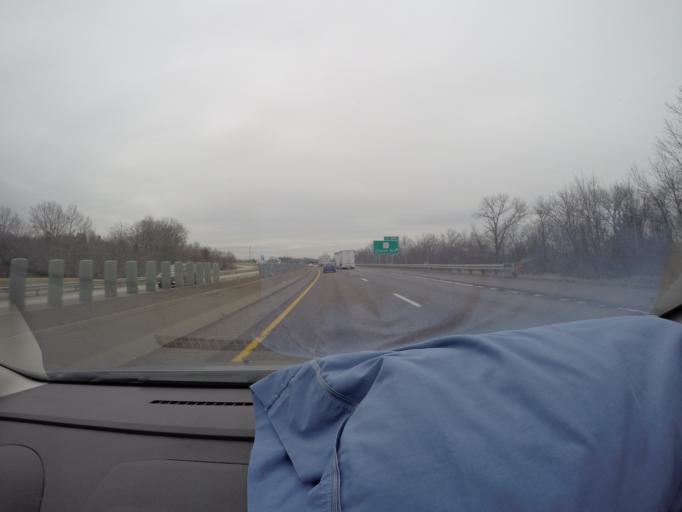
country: US
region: Missouri
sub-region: Saint Charles County
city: Wentzville
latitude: 38.8068
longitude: -90.8618
